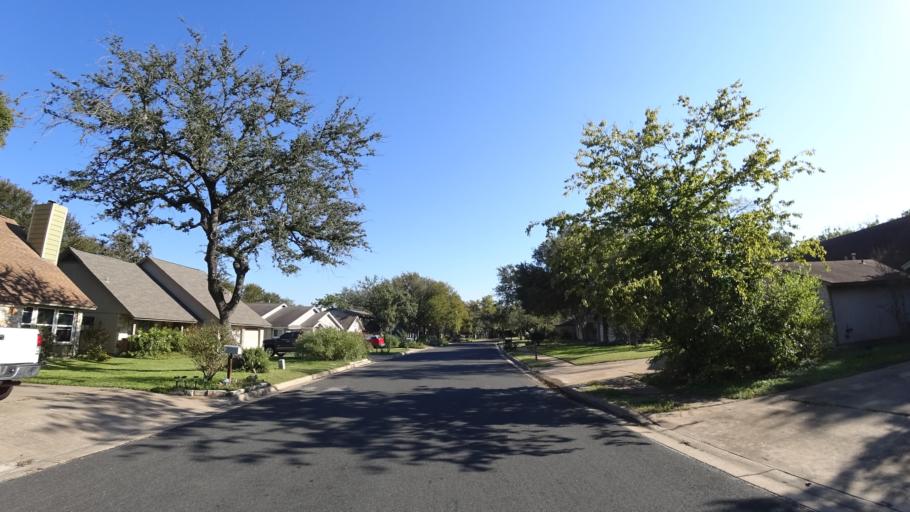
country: US
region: Texas
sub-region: Travis County
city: Shady Hollow
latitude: 30.2152
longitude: -97.8485
